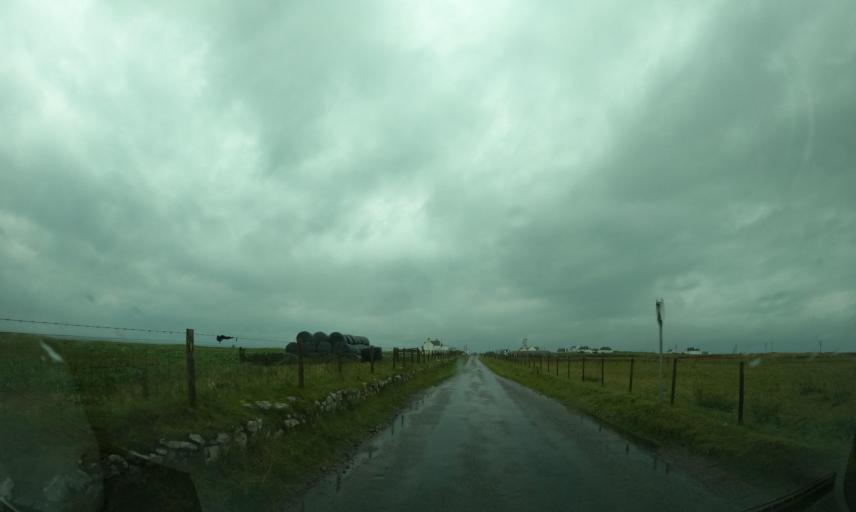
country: GB
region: Scotland
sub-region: Eilean Siar
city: Barra
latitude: 56.5052
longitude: -6.8084
